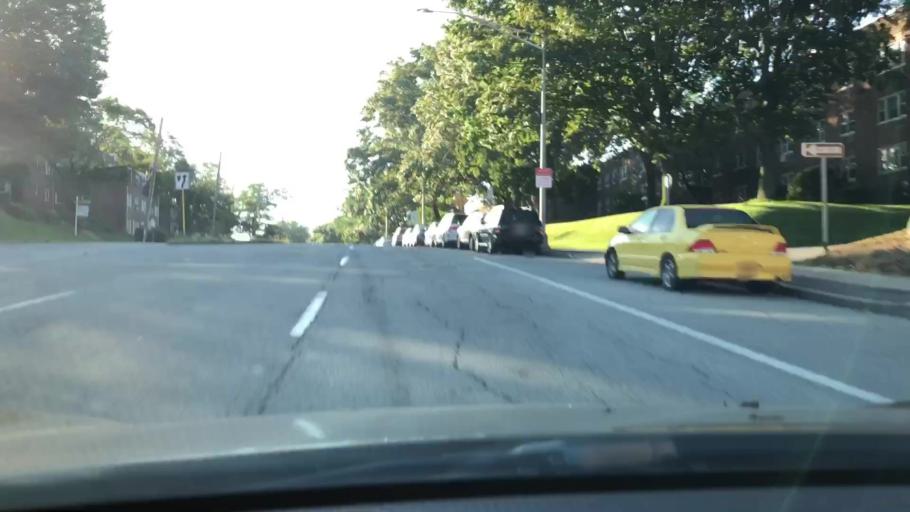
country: US
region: New York
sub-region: Westchester County
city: Tuckahoe
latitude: 40.9523
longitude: -73.8418
